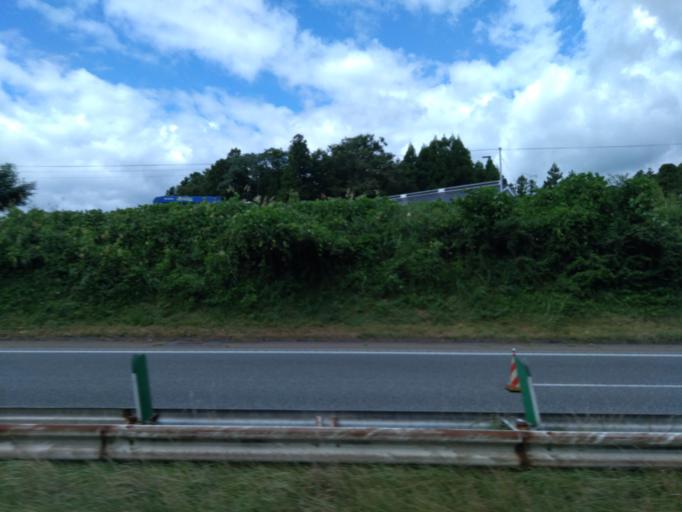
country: JP
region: Miyagi
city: Furukawa
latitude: 38.6545
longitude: 140.9711
